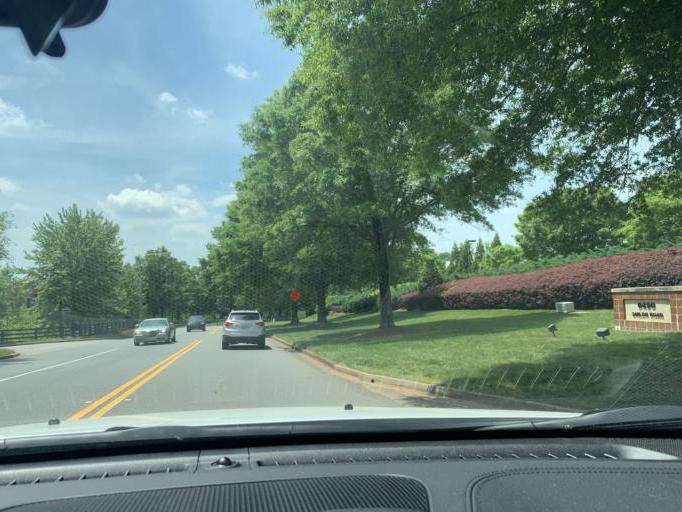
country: US
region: Georgia
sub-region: Fulton County
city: Johns Creek
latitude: 34.1084
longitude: -84.2098
